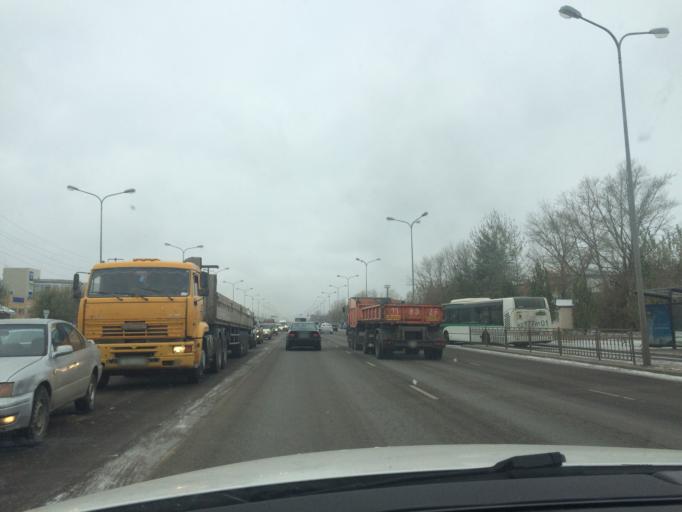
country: KZ
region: Astana Qalasy
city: Astana
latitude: 51.1791
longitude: 71.4681
